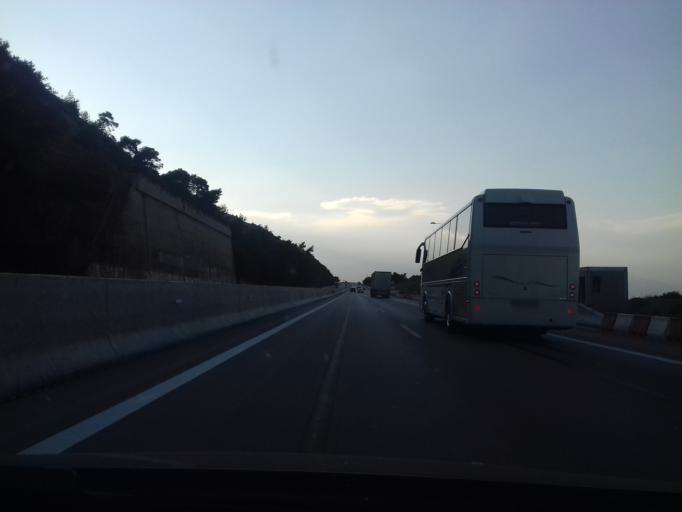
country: GR
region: West Greece
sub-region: Nomos Achaias
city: Siliveniotika
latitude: 38.1654
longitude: 22.3325
